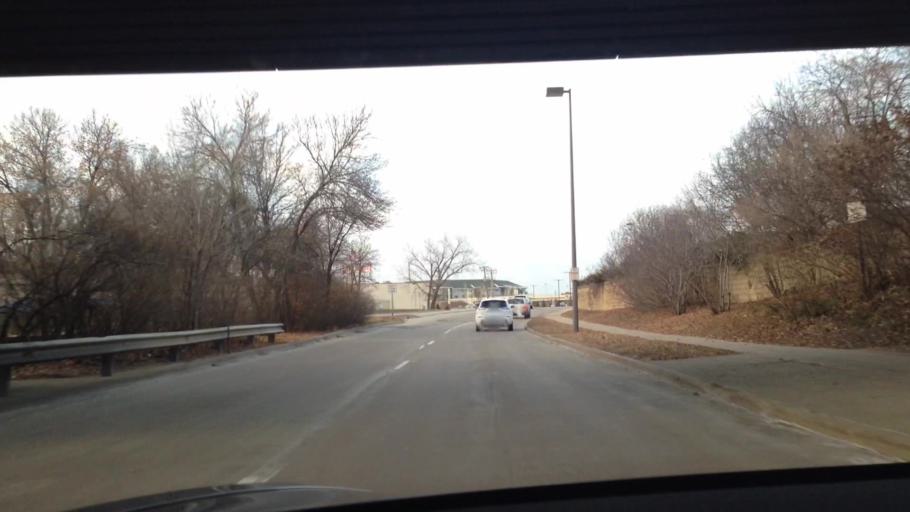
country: US
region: Minnesota
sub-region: Hennepin County
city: Saint Louis Park
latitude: 44.9343
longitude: -93.3677
